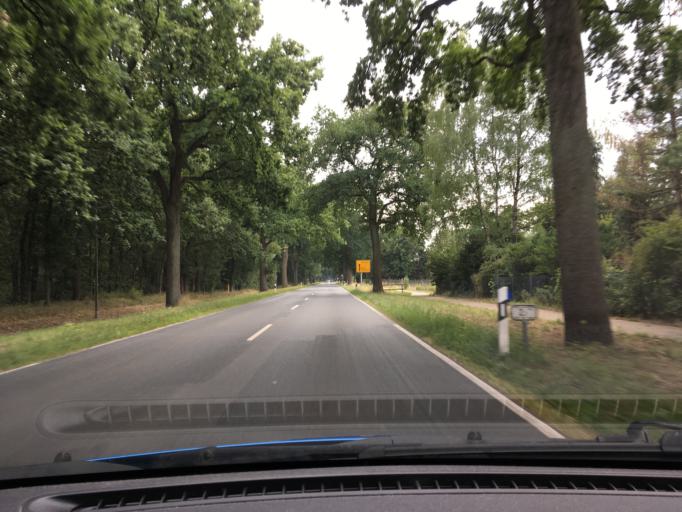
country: DE
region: Lower Saxony
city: Adelheidsdorf
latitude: 52.5565
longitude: 10.0571
